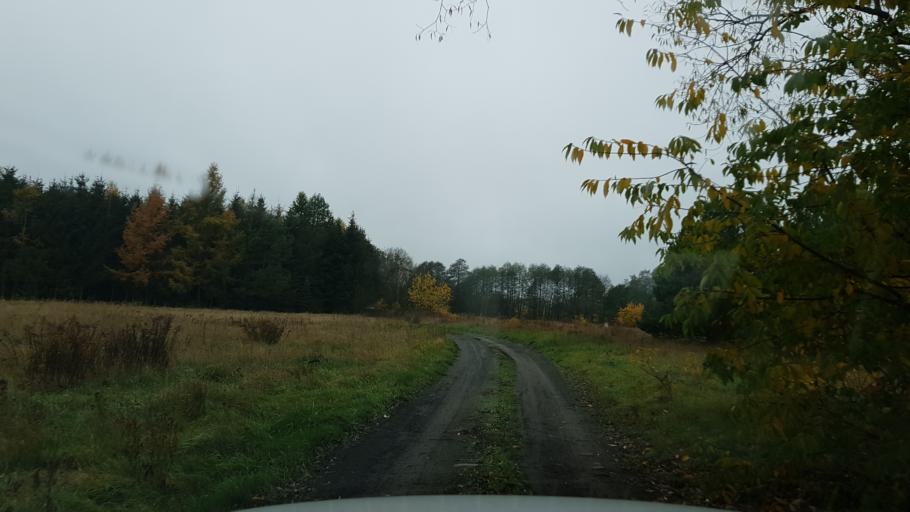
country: PL
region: West Pomeranian Voivodeship
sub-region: Powiat goleniowski
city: Goleniow
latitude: 53.6063
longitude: 14.7506
